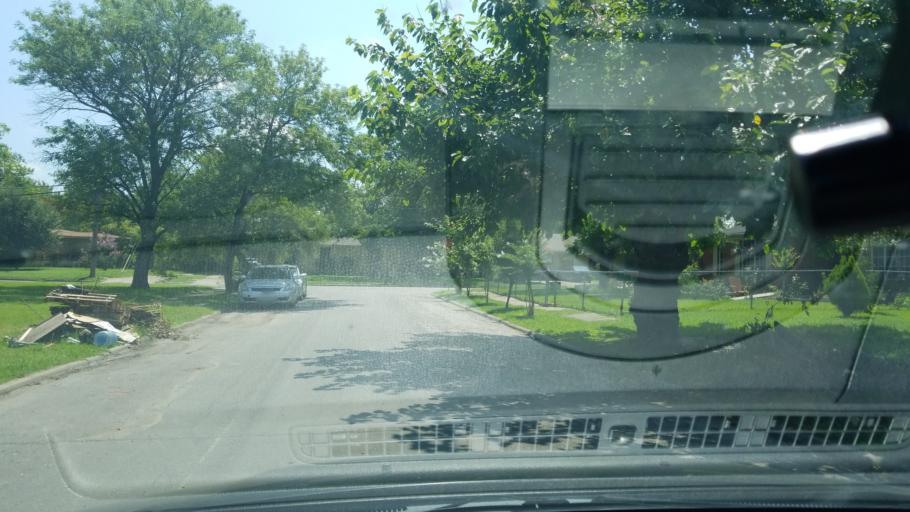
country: US
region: Texas
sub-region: Dallas County
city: Balch Springs
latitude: 32.7436
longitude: -96.6877
